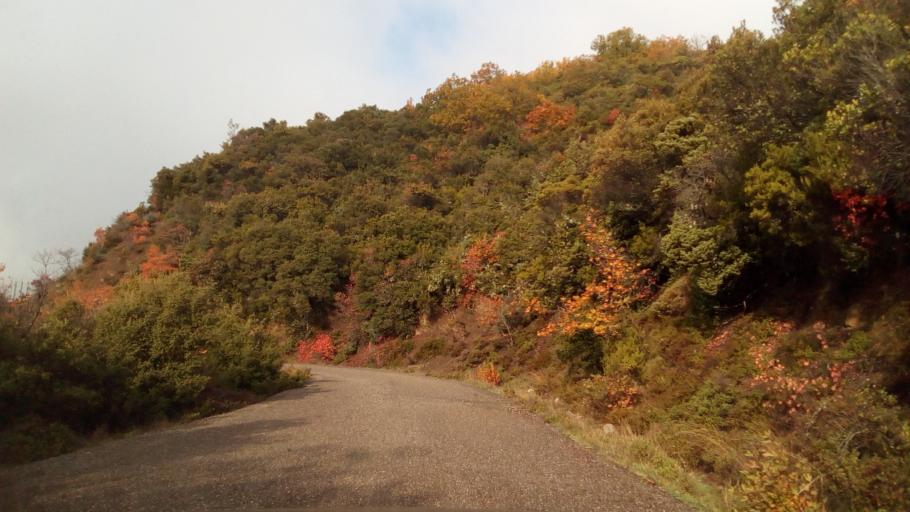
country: GR
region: West Greece
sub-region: Nomos Aitolias kai Akarnanias
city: Nafpaktos
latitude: 38.5189
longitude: 21.9457
